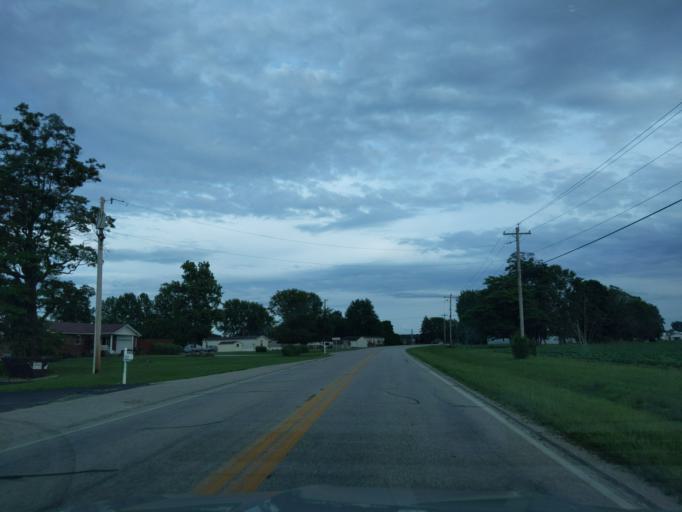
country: US
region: Indiana
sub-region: Ripley County
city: Sunman
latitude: 39.2681
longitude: -85.0963
